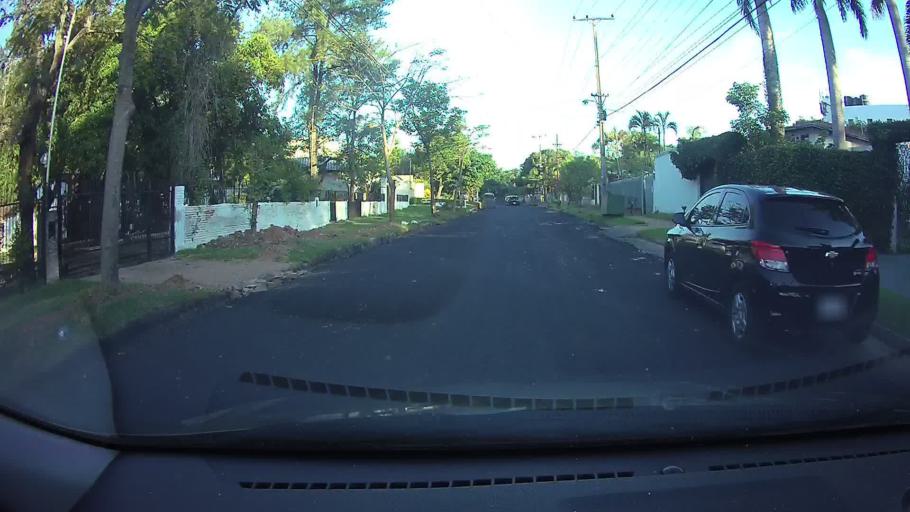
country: PY
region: Central
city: Fernando de la Mora
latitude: -25.2624
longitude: -57.5137
